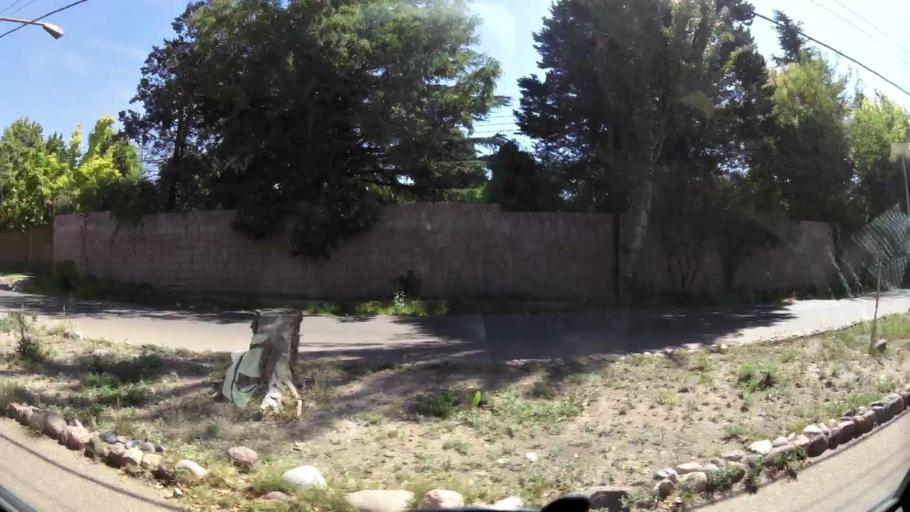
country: AR
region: Mendoza
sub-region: Departamento de Godoy Cruz
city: Godoy Cruz
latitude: -32.9669
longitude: -68.8690
